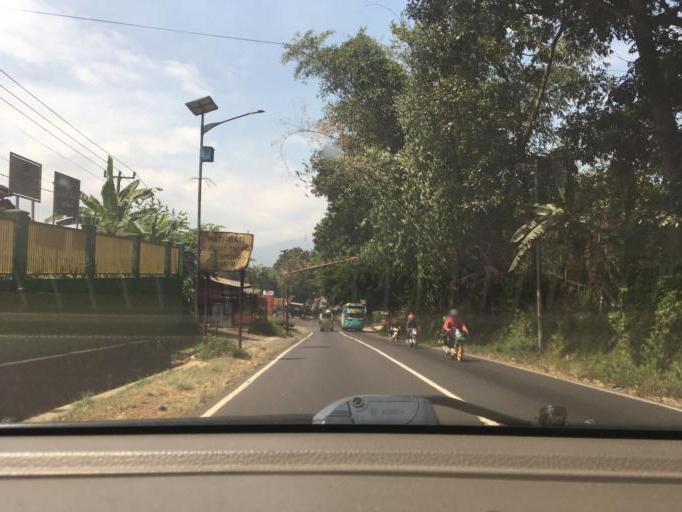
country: ID
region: West Java
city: Tagog
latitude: -7.1186
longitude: 108.1338
